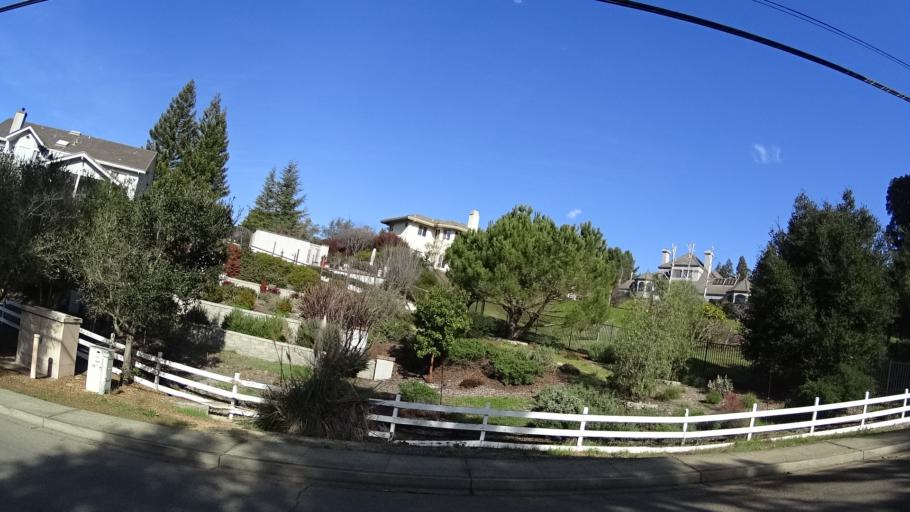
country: US
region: California
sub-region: Alameda County
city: Fairview
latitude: 37.6623
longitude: -122.0286
